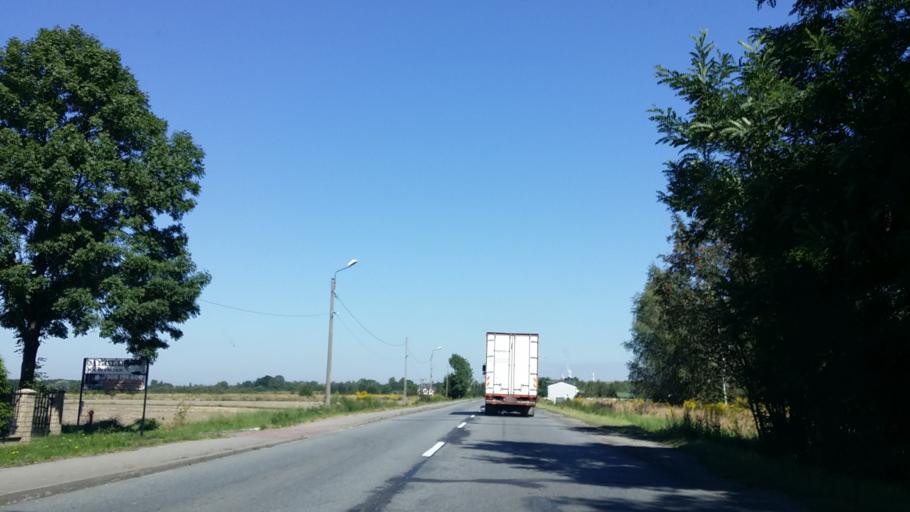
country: PL
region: Silesian Voivodeship
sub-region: Powiat bierunsko-ledzinski
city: Chelm Slaski
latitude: 50.1221
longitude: 19.2002
